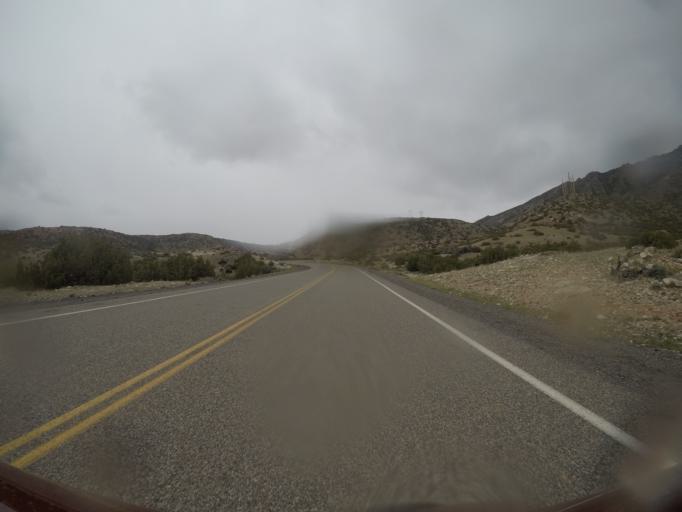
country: US
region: Wyoming
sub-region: Big Horn County
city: Lovell
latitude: 45.0330
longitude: -108.2612
